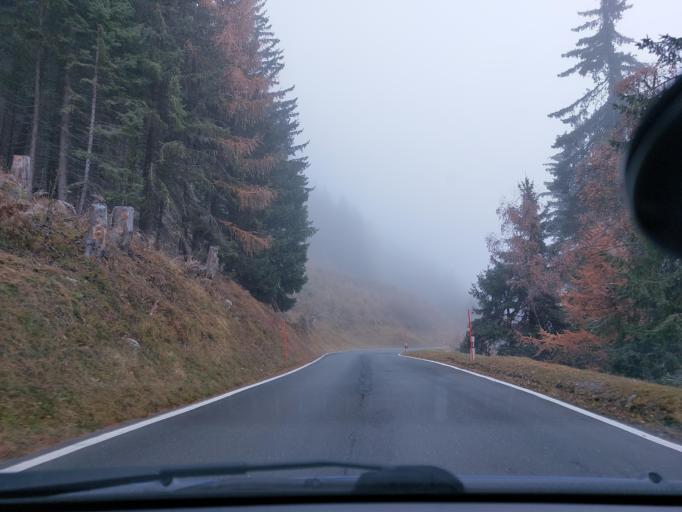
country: CH
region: Valais
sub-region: Conthey District
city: Basse-Nendaz
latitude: 46.1612
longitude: 7.3126
